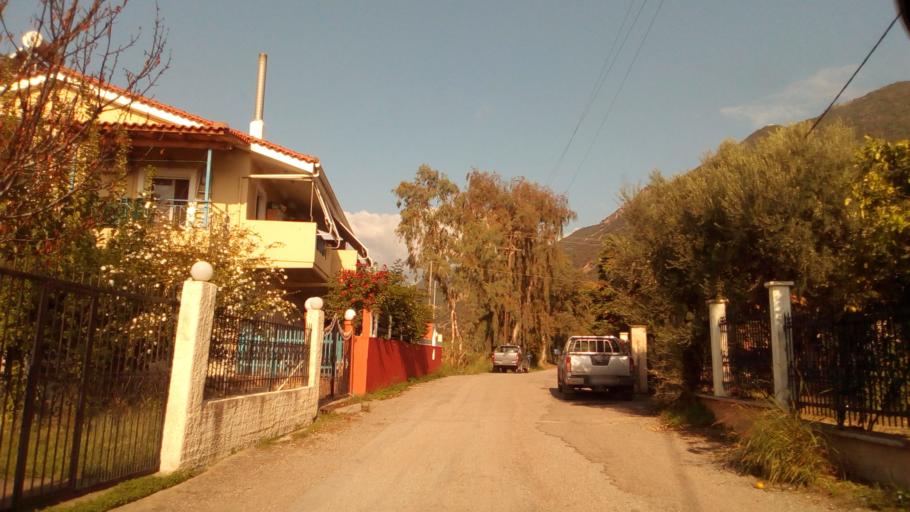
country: GR
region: West Greece
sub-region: Nomos Achaias
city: Kamarai
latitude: 38.3946
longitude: 22.0050
